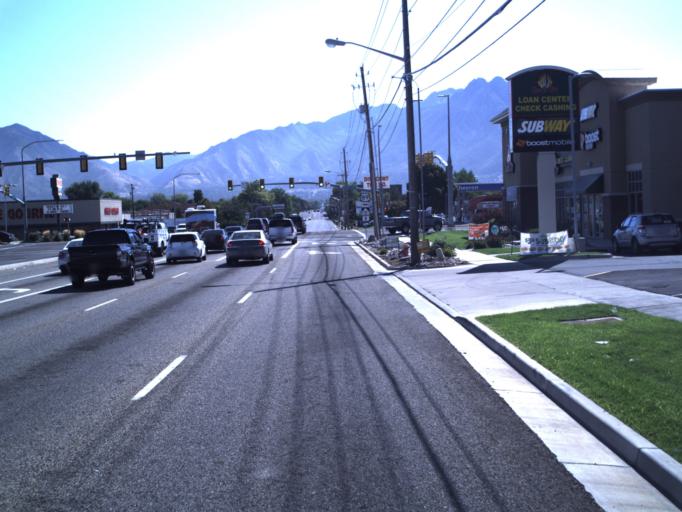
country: US
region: Utah
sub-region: Salt Lake County
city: Murray
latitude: 40.6742
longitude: -111.8894
